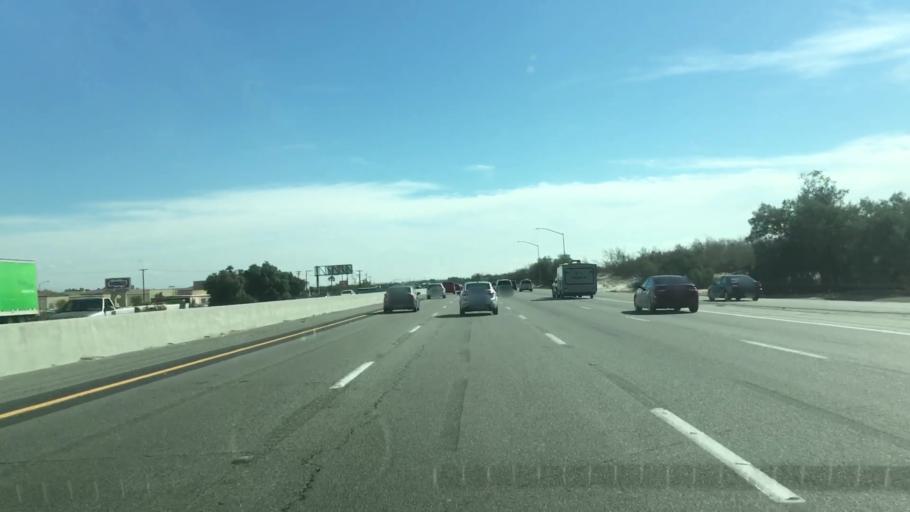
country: US
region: California
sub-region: Riverside County
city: Thousand Palms
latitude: 33.8149
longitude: -116.4022
